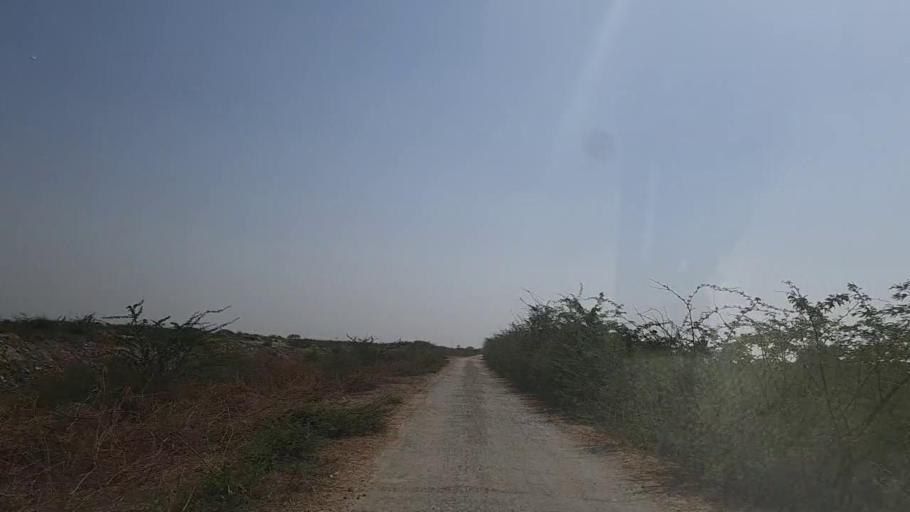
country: PK
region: Sindh
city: Naukot
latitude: 24.6297
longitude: 69.2714
